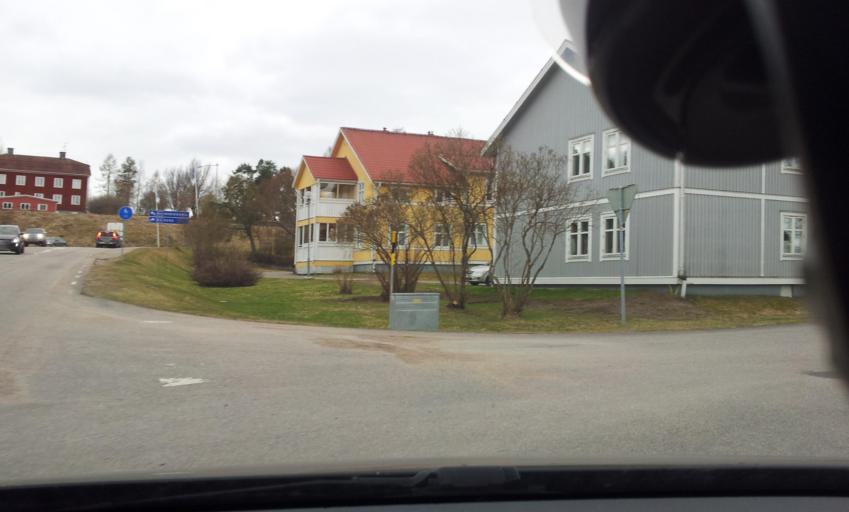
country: SE
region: Gaevleborg
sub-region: Ljusdals Kommun
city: Farila
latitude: 61.8026
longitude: 15.8502
